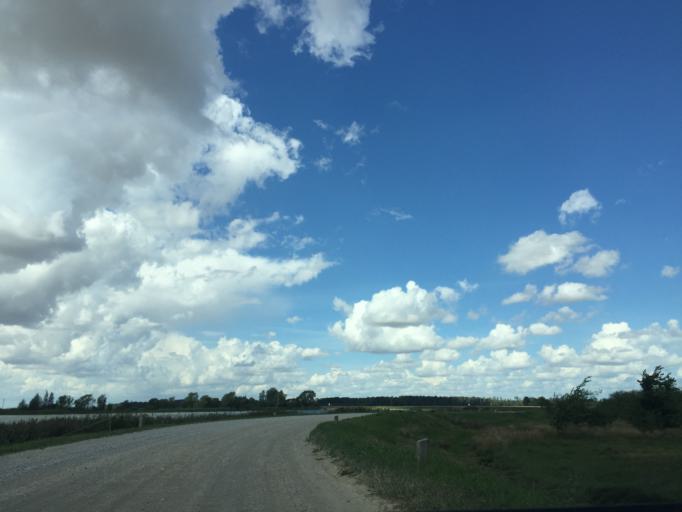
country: LV
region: Rundales
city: Pilsrundale
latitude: 56.3003
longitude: 23.9884
